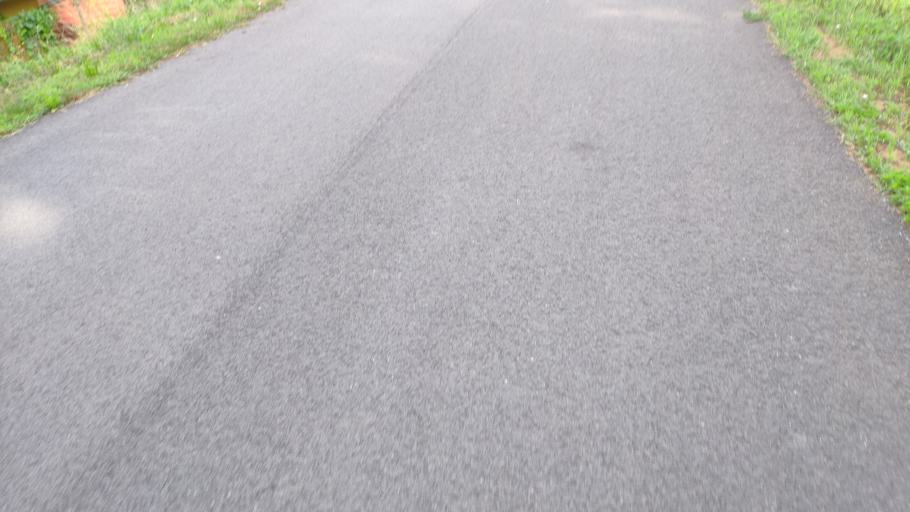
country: SK
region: Nitriansky
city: Kolarovo
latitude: 47.9179
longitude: 18.0038
